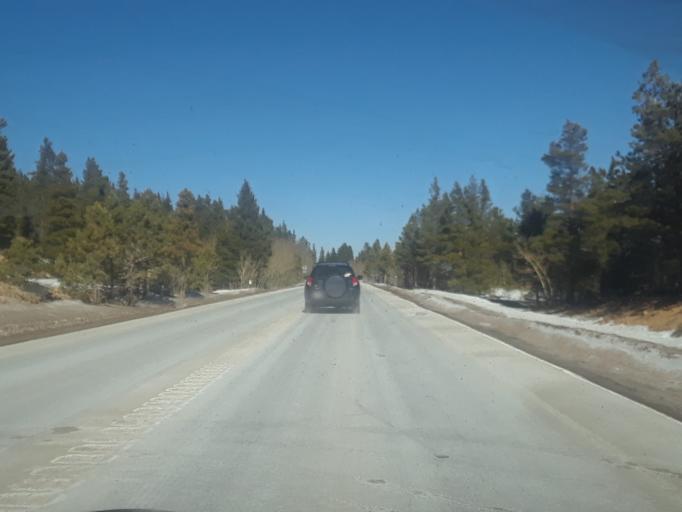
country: US
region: Colorado
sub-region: Boulder County
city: Nederland
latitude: 40.0857
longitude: -105.4977
